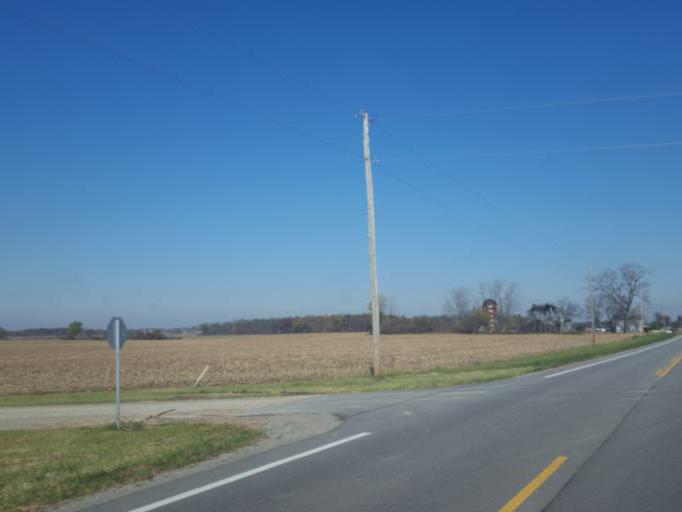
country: US
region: Ohio
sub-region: Wyandot County
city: Upper Sandusky
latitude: 40.9298
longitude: -83.2729
